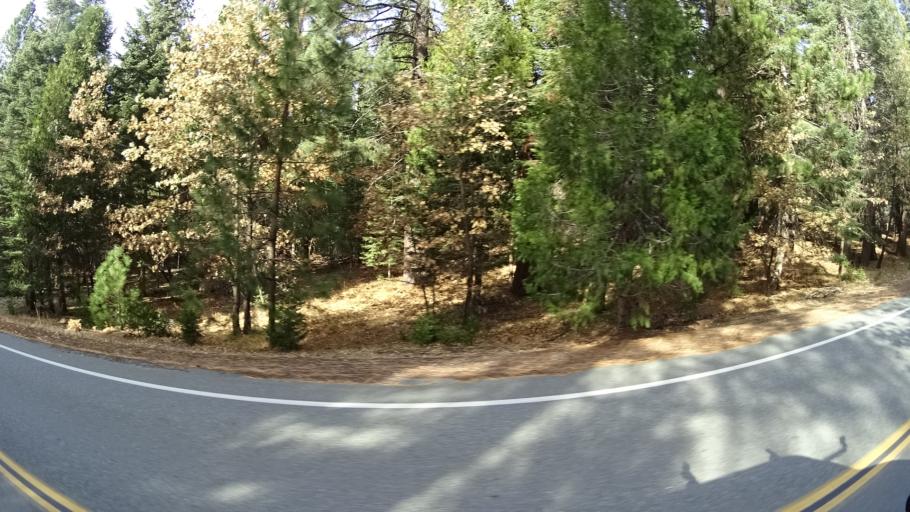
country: US
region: California
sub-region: Siskiyou County
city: Weed
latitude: 41.3819
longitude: -122.3907
